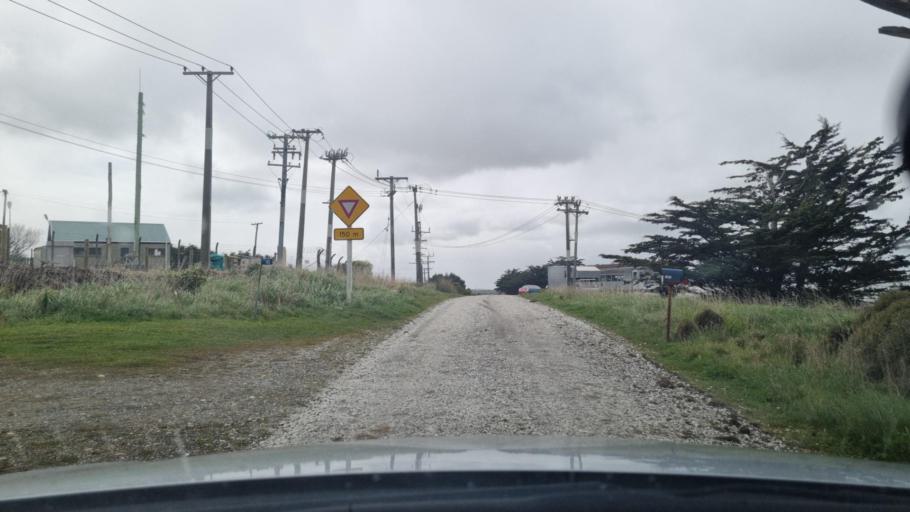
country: NZ
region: Southland
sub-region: Invercargill City
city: Bluff
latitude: -46.5854
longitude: 168.3038
